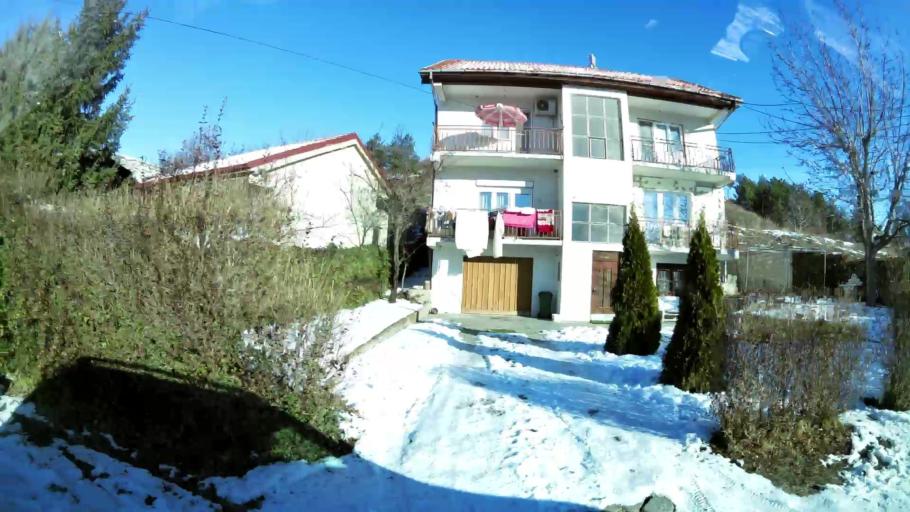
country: MK
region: Saraj
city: Saraj
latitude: 42.0110
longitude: 21.3396
